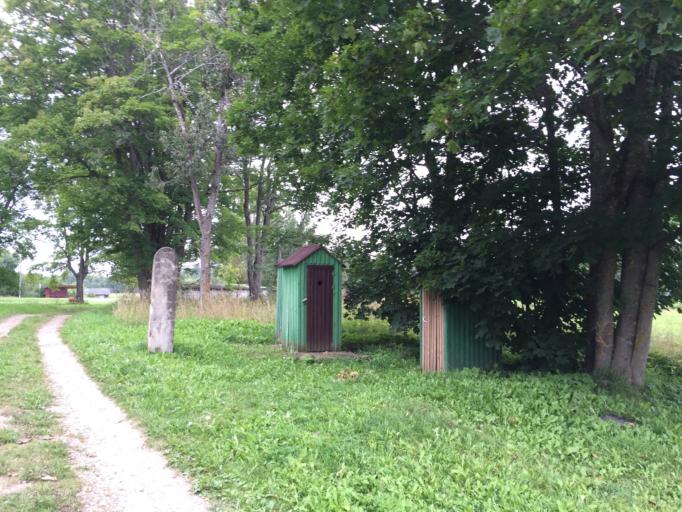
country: LV
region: Zilupes
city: Zilupe
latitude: 56.2890
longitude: 28.1600
